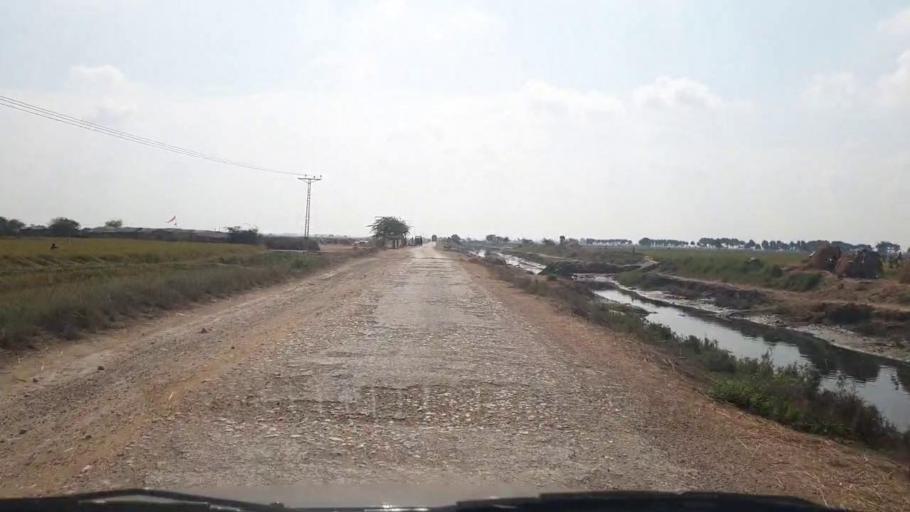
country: PK
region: Sindh
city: Kario
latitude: 24.6295
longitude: 68.5516
